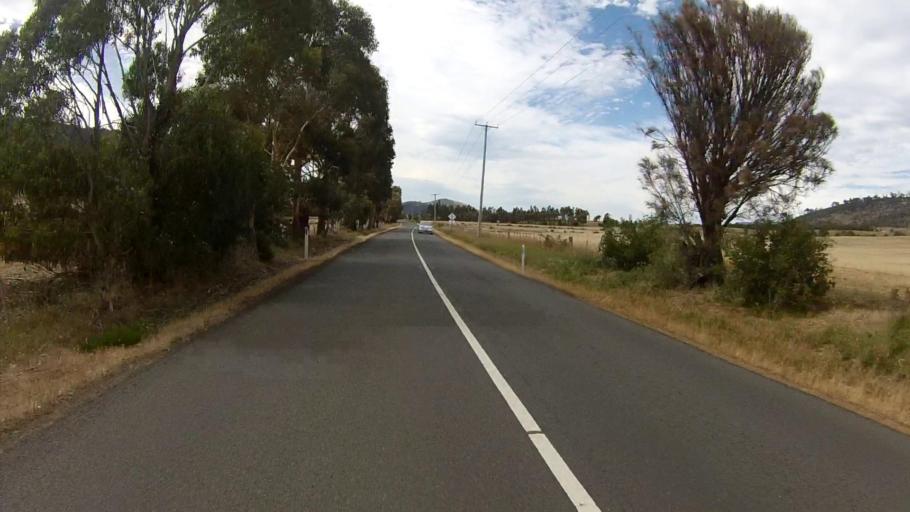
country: AU
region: Tasmania
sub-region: Brighton
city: Old Beach
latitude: -42.7126
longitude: 147.3794
